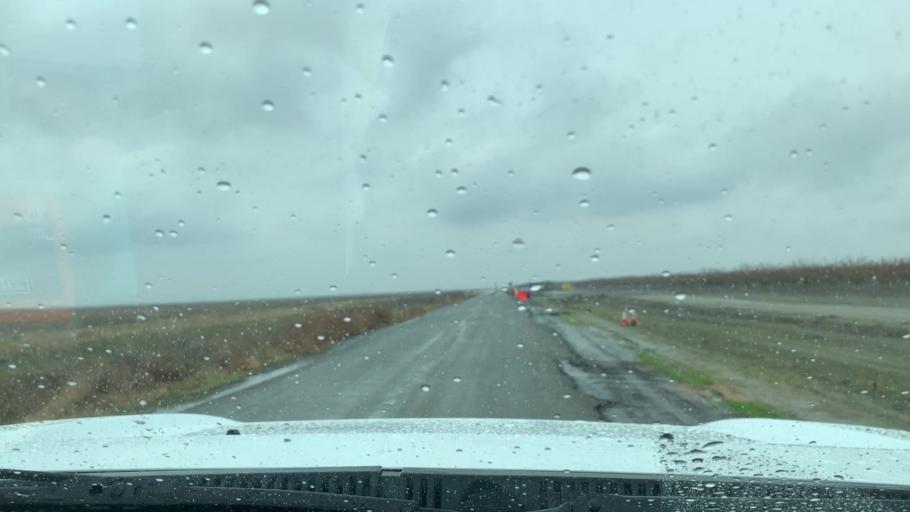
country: US
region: California
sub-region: Kings County
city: Corcoran
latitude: 36.0073
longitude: -119.4946
